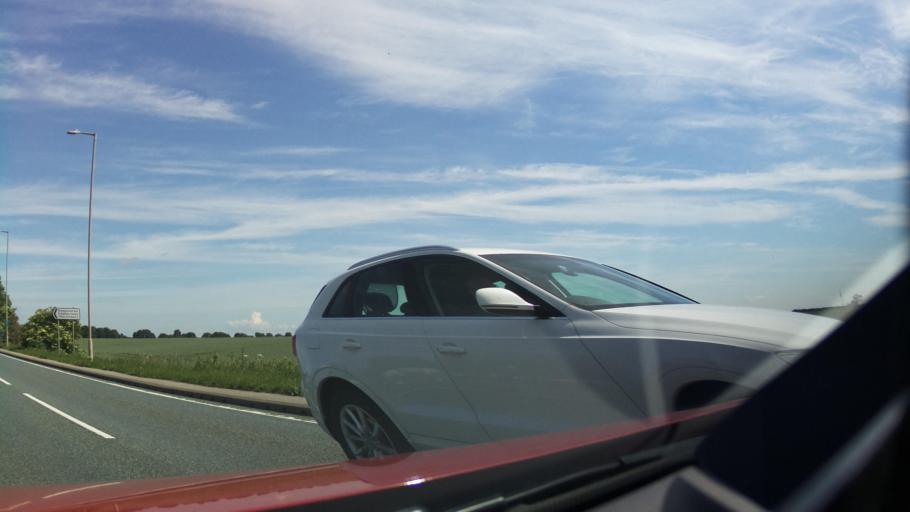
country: GB
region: England
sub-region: Lincolnshire
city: Burton
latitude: 53.2846
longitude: -0.5403
